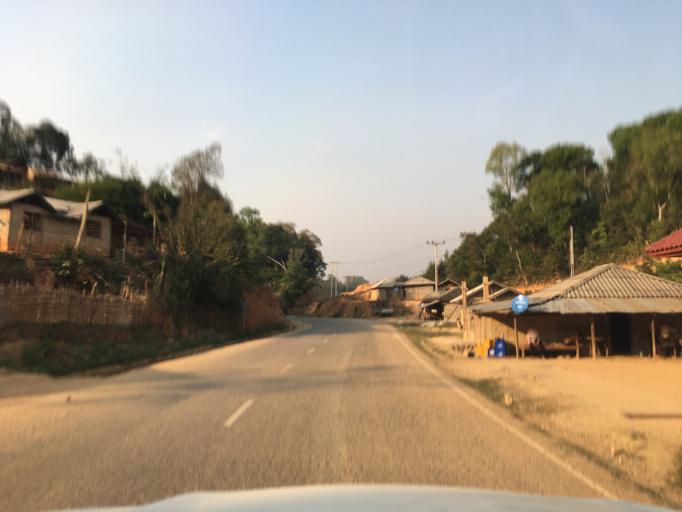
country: LA
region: Houaphan
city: Xam Nua
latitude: 20.5965
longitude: 104.0681
